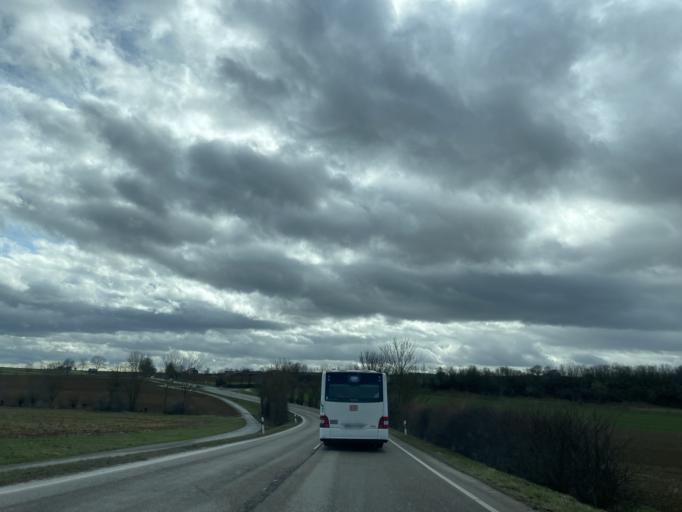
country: DE
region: Baden-Wuerttemberg
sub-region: Regierungsbezirk Stuttgart
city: Hemmingen
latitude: 48.8441
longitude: 9.0036
